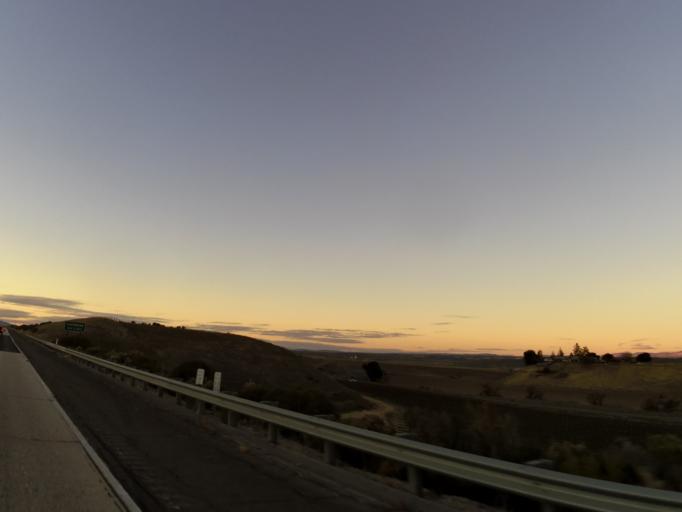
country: US
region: California
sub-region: Monterey County
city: King City
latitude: 36.0829
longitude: -121.0060
